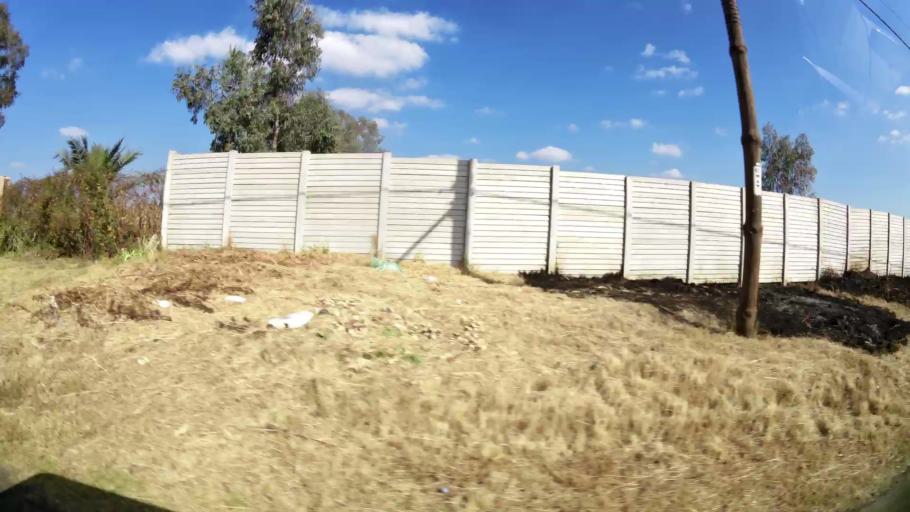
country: ZA
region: Gauteng
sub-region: Ekurhuleni Metropolitan Municipality
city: Benoni
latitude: -26.0972
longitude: 28.3498
